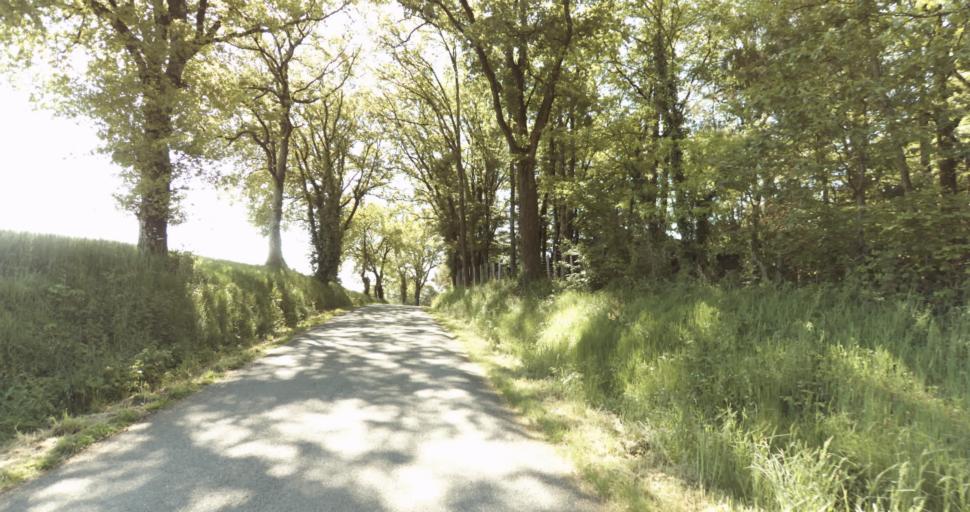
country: FR
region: Limousin
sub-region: Departement de la Haute-Vienne
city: Le Vigen
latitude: 45.7156
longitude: 1.2895
